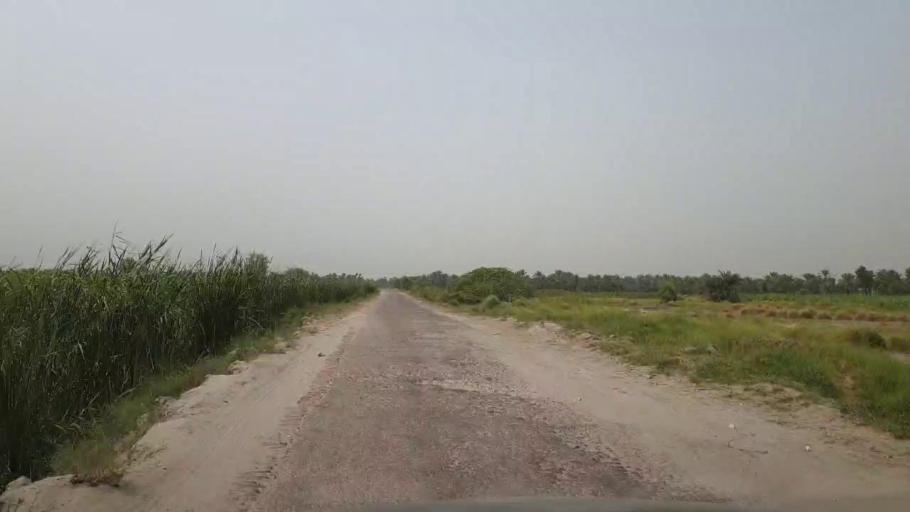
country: PK
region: Sindh
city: Gambat
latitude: 27.3855
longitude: 68.5486
